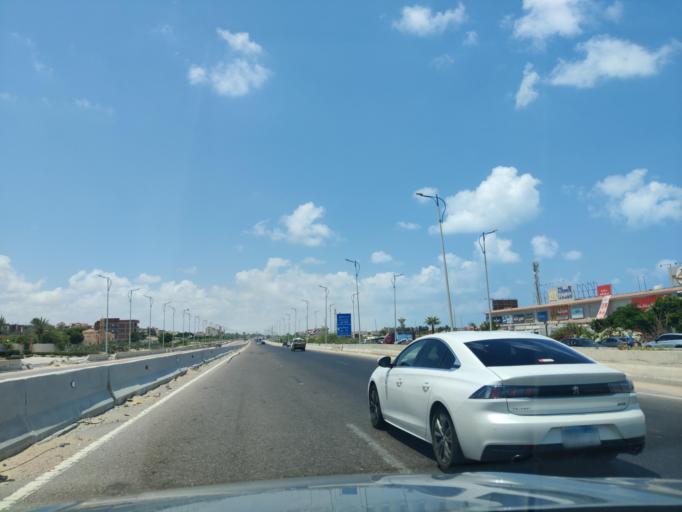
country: EG
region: Alexandria
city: Alexandria
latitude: 30.9785
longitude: 29.5751
